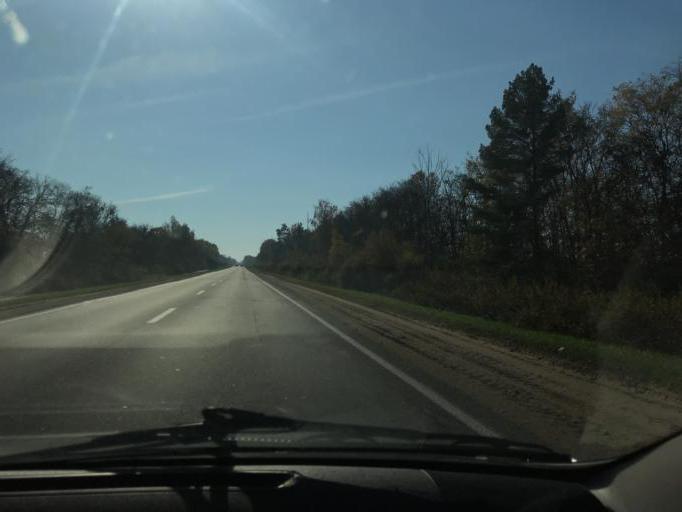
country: BY
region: Minsk
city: Starobin
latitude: 52.7947
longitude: 27.4646
